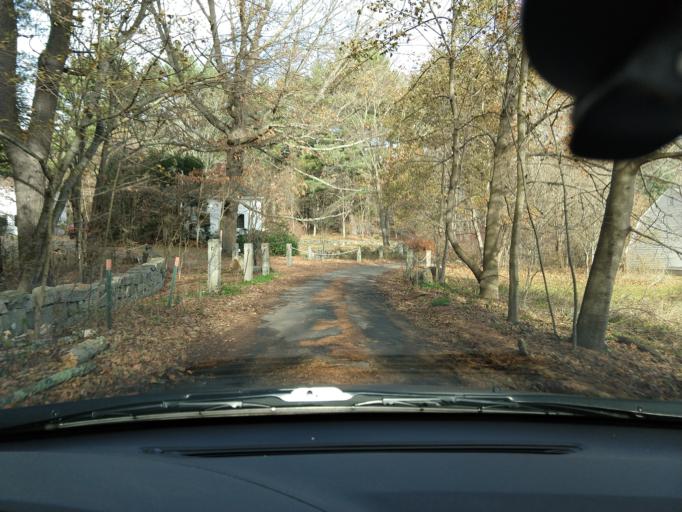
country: US
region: Massachusetts
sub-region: Middlesex County
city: Bedford
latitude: 42.5209
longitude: -71.3035
